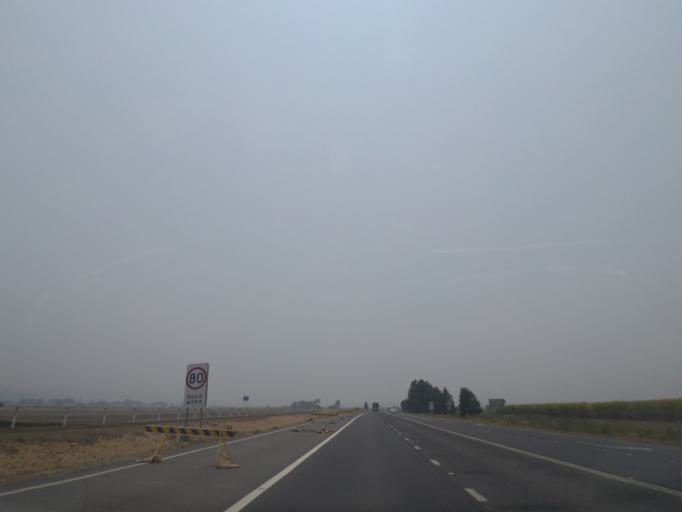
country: AU
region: New South Wales
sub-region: Clarence Valley
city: Maclean
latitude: -29.3921
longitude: 153.2398
